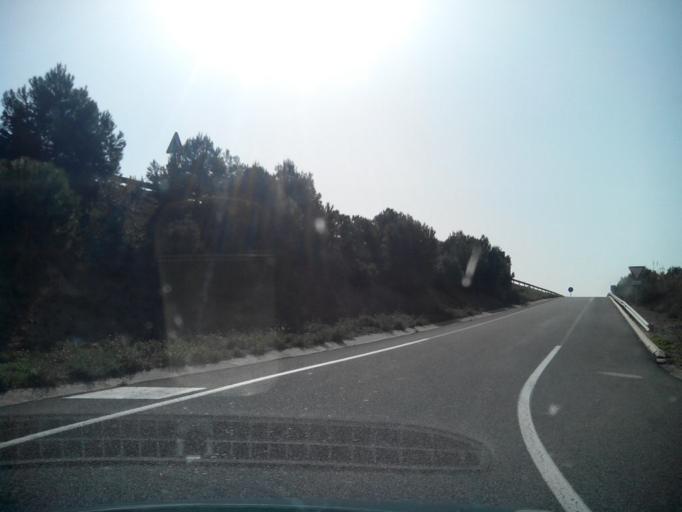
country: ES
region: Catalonia
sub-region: Provincia de Tarragona
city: Alcover
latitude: 41.2531
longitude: 1.1731
